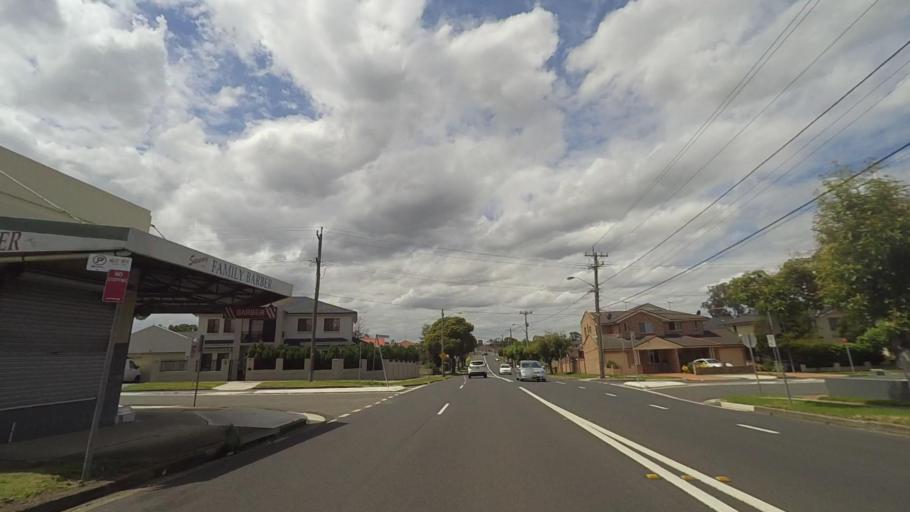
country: AU
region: New South Wales
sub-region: Fairfield
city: Fairfield Heights
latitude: -33.8659
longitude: 150.9498
